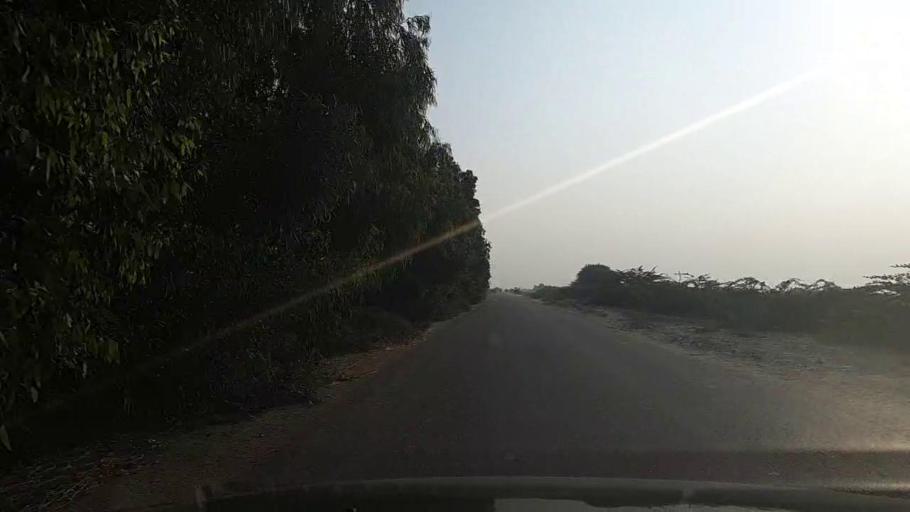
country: PK
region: Sindh
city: Mirpur Sakro
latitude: 24.4981
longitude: 67.8128
